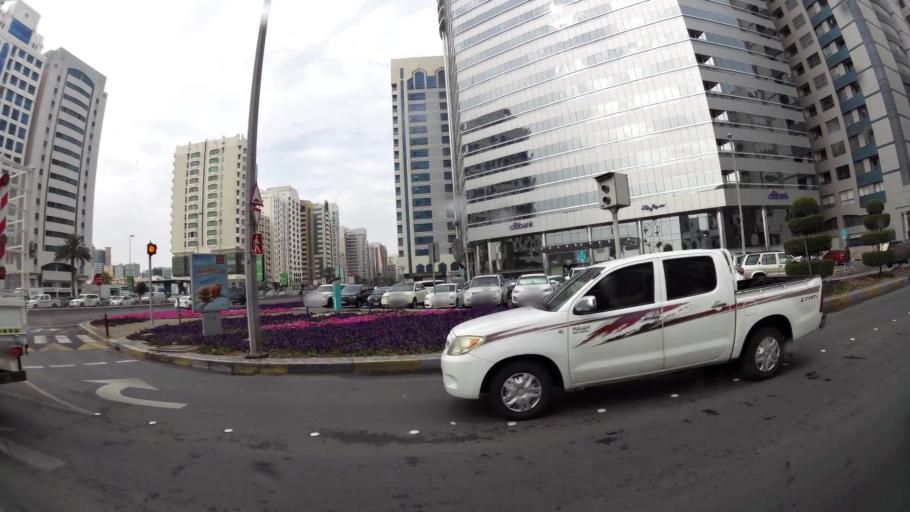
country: AE
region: Abu Dhabi
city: Abu Dhabi
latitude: 24.4833
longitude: 54.3755
